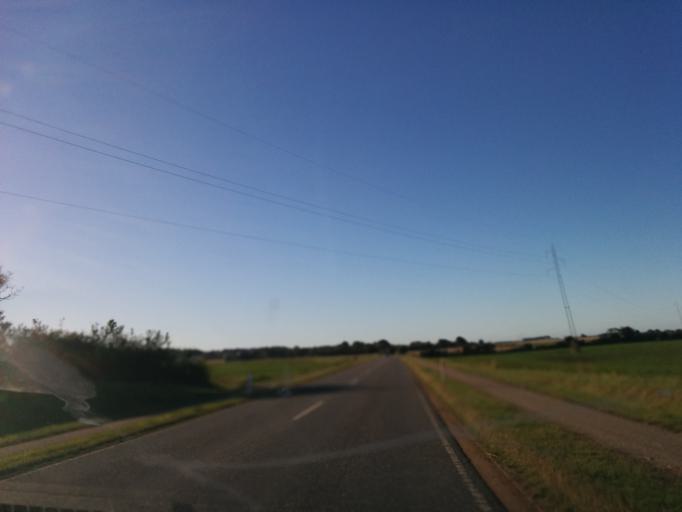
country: DK
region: South Denmark
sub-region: Kolding Kommune
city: Sonder Bjert
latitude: 55.4447
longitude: 9.5562
